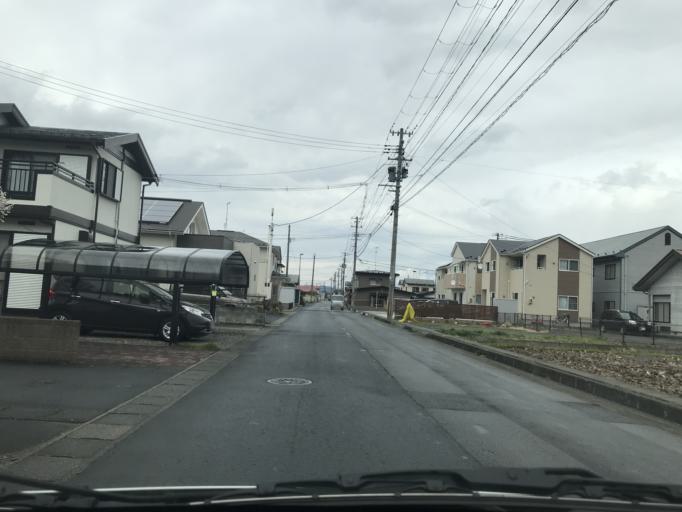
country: JP
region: Iwate
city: Mizusawa
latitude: 39.1503
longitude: 141.1381
